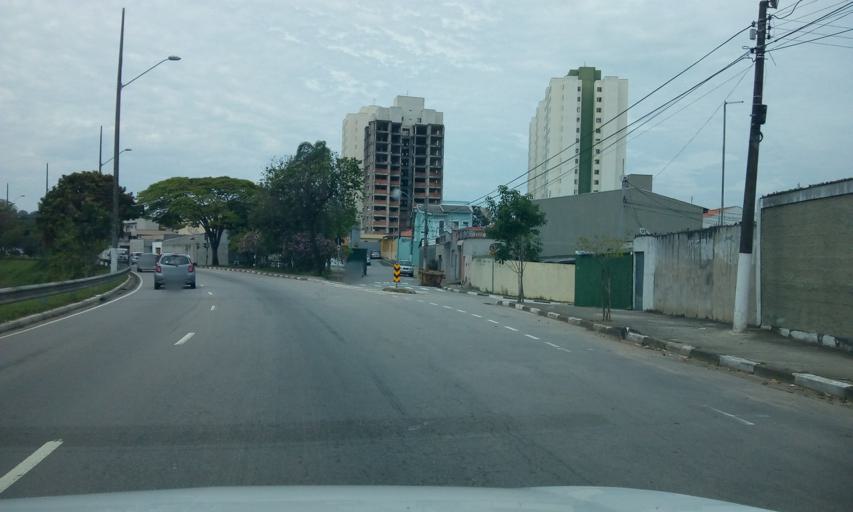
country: BR
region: Sao Paulo
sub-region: Jundiai
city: Jundiai
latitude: -23.2163
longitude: -46.8752
